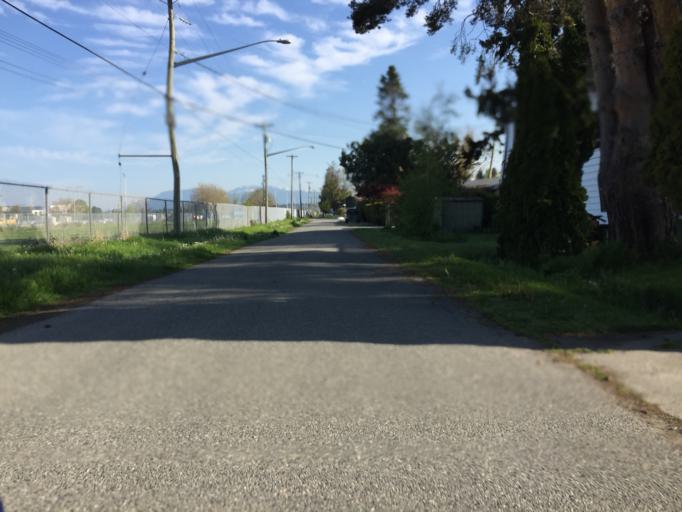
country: CA
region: British Columbia
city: Richmond
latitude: 49.1869
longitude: -123.1503
